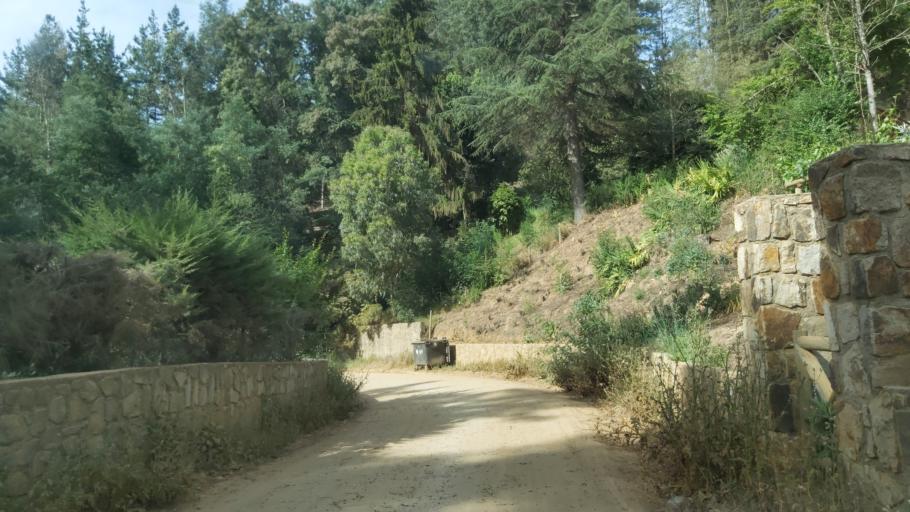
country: CL
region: Maule
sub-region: Provincia de Talca
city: Constitucion
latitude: -34.8432
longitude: -72.0407
